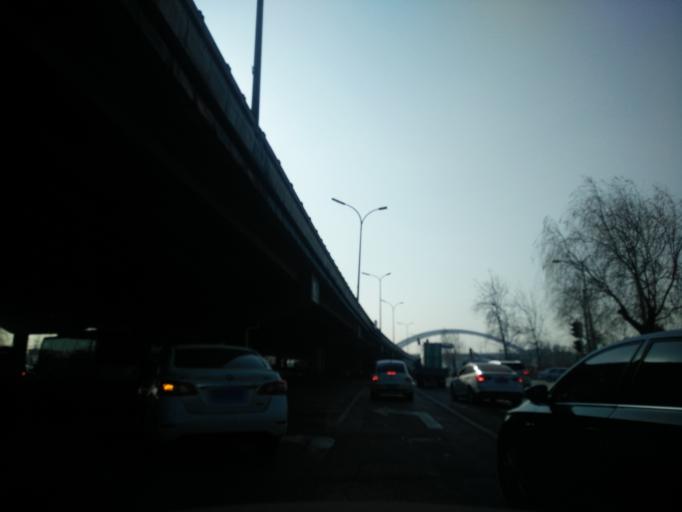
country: CN
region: Beijing
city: Jiugong
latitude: 39.8478
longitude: 116.4787
